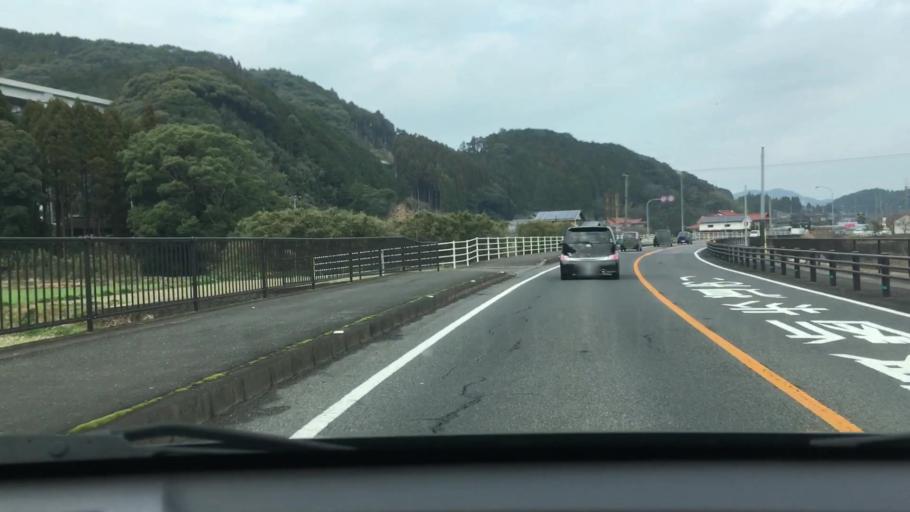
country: JP
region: Saga Prefecture
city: Imaricho-ko
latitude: 33.3238
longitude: 129.9289
